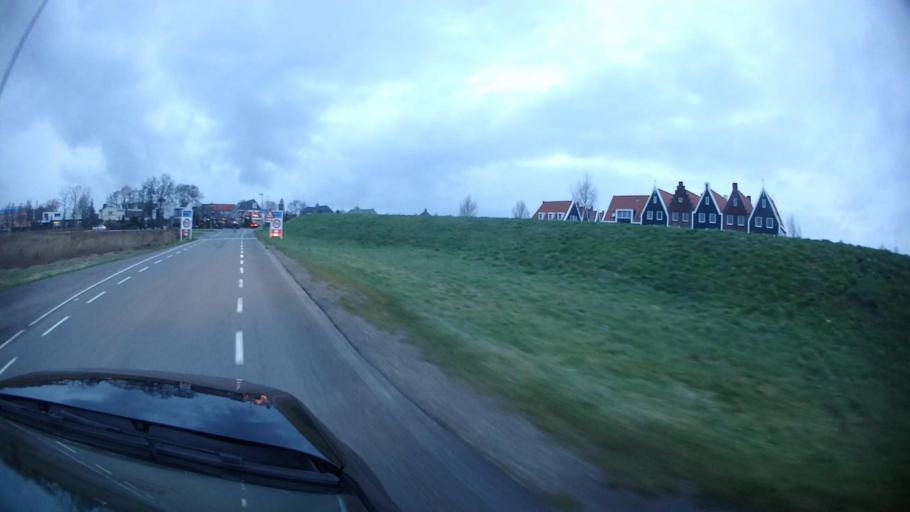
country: NL
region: North Holland
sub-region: Gemeente Edam-Volendam
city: Volendam
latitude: 52.4906
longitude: 5.0593
